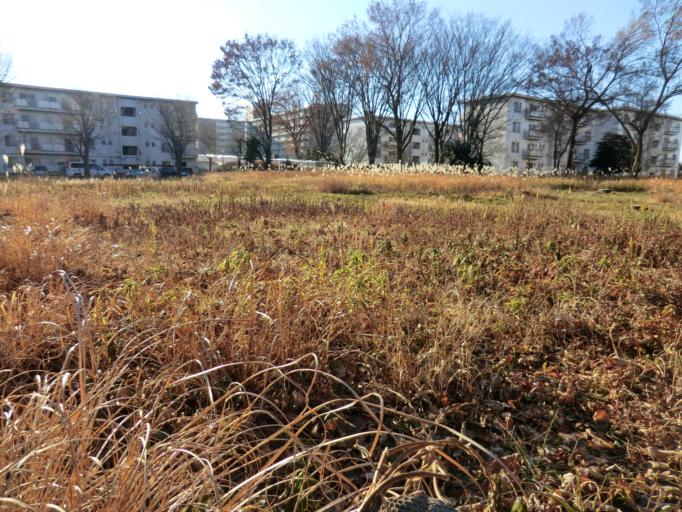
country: JP
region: Ibaraki
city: Naka
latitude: 36.0825
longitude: 140.1076
